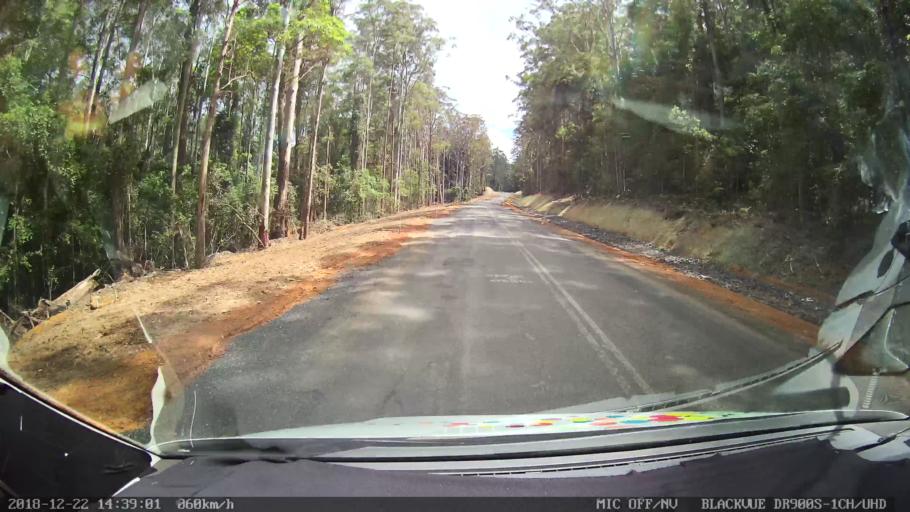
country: AU
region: New South Wales
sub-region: Bellingen
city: Dorrigo
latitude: -30.1429
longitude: 152.5945
